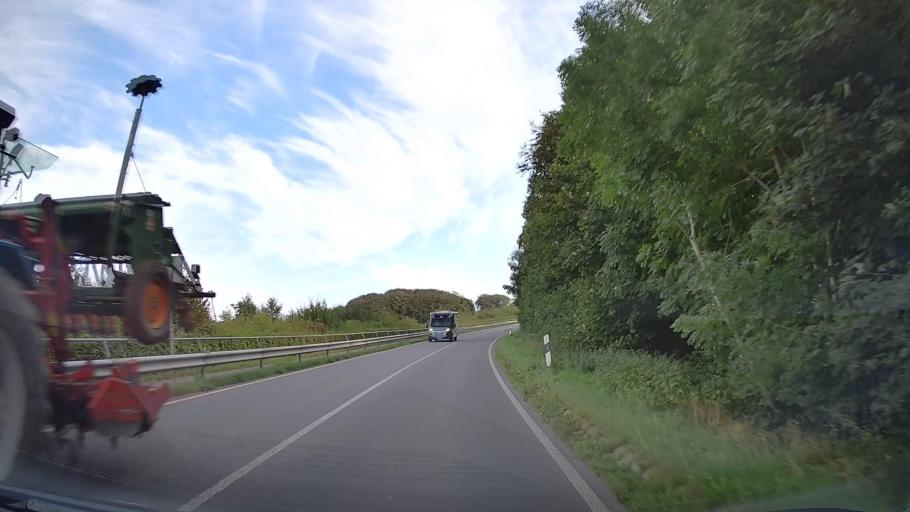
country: DE
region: Schleswig-Holstein
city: Westerholz
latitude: 54.8192
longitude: 9.6685
